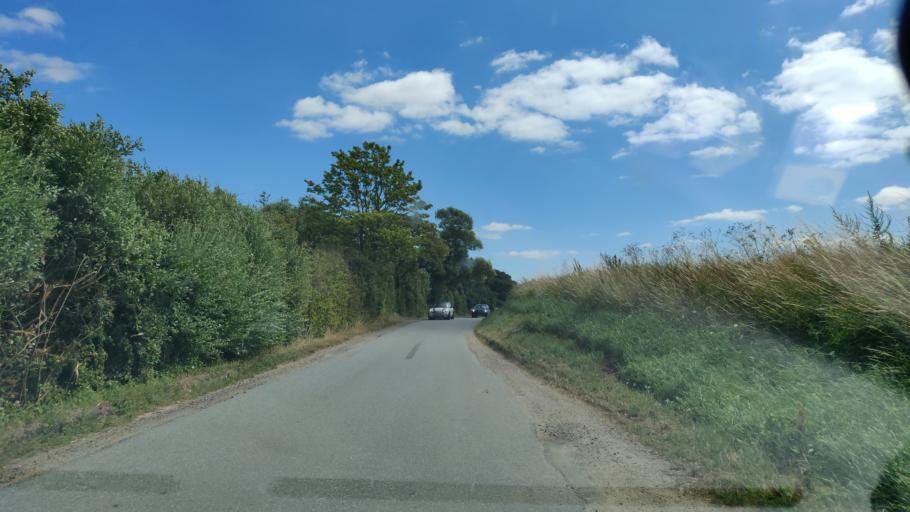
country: DK
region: South Denmark
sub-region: Fredericia Kommune
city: Taulov
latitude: 55.5245
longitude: 9.5452
